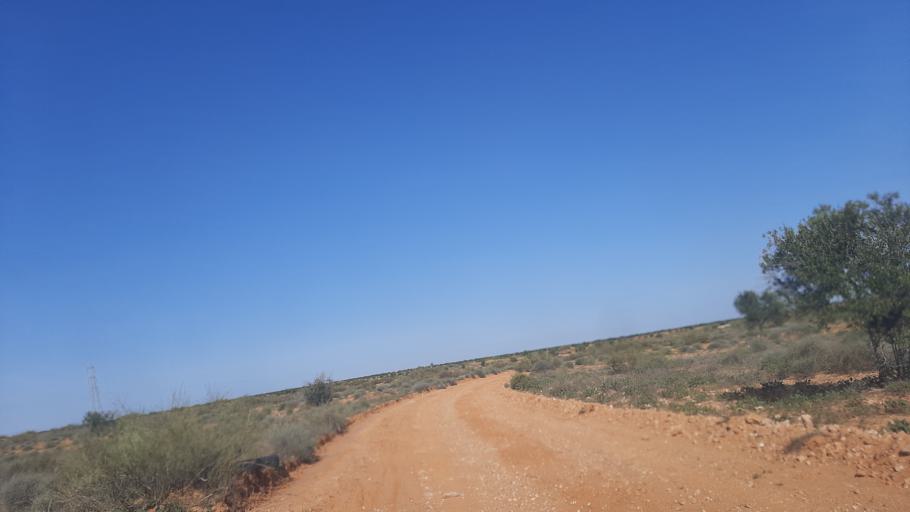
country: TN
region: Madanin
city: Medenine
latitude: 33.2758
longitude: 10.7720
